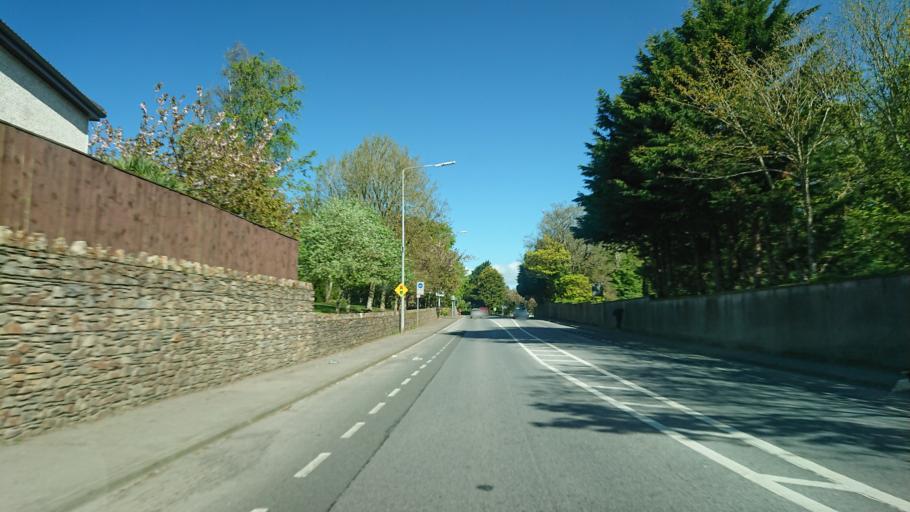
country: IE
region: Munster
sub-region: Waterford
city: Waterford
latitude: 52.2433
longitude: -7.0708
